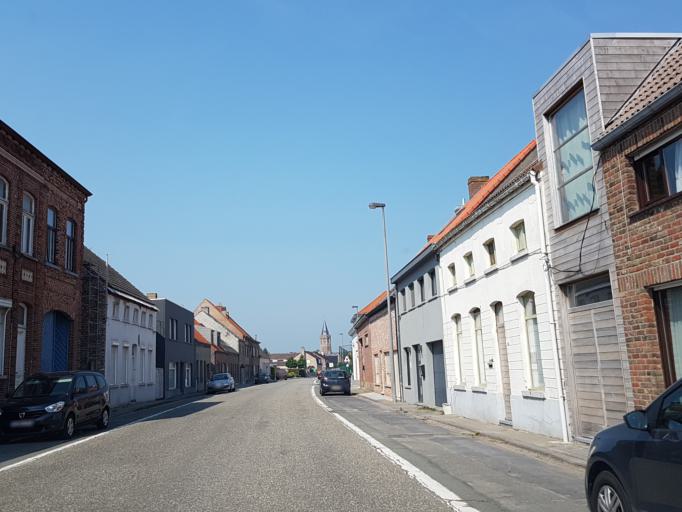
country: BE
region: Flanders
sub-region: Provincie West-Vlaanderen
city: Jabbeke
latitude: 51.2098
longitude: 3.0761
